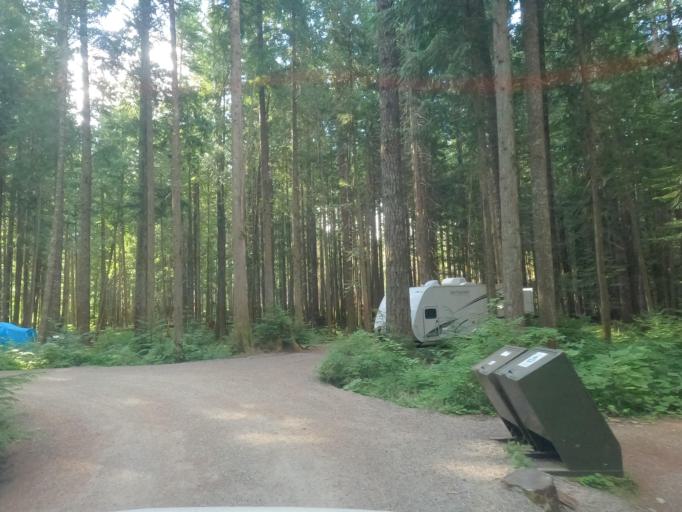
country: CA
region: British Columbia
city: Whistler
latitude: 50.0633
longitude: -123.0996
